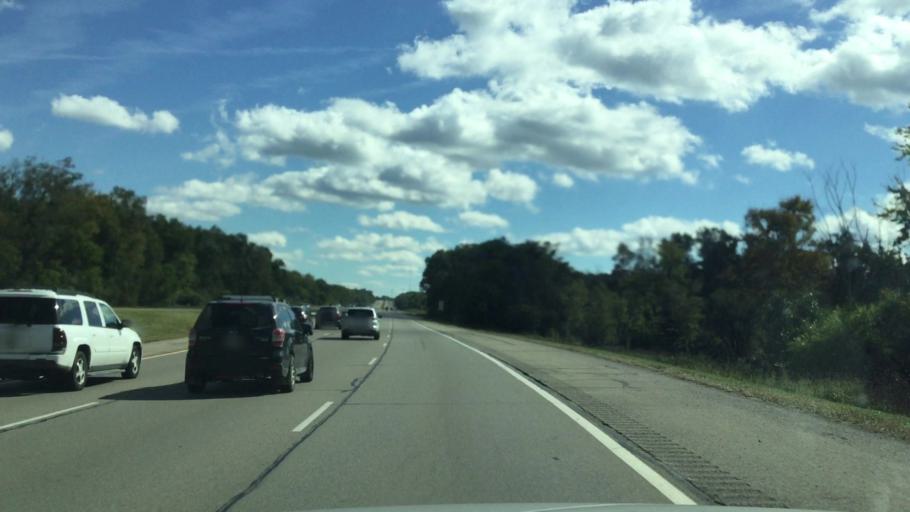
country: US
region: Michigan
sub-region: Oakland County
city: Holly
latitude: 42.8094
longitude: -83.5678
